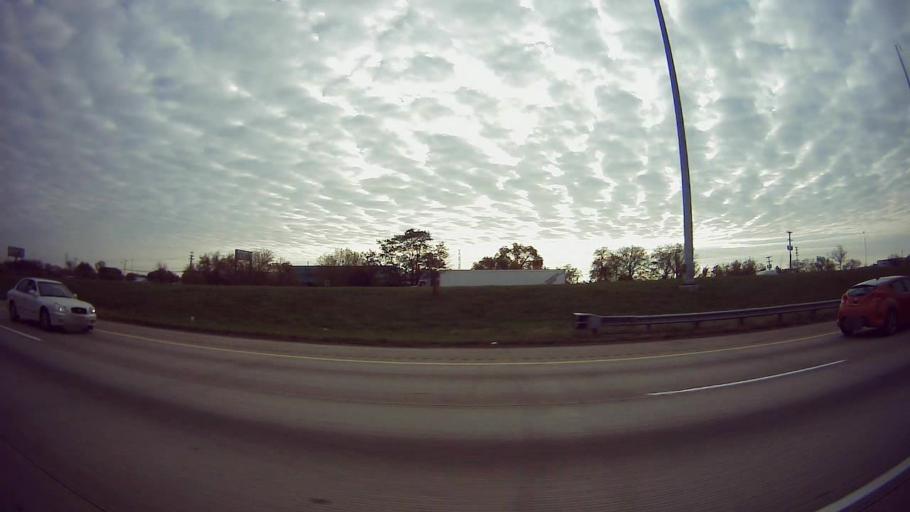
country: US
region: Michigan
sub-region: Wayne County
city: Allen Park
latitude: 42.2774
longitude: -83.2031
